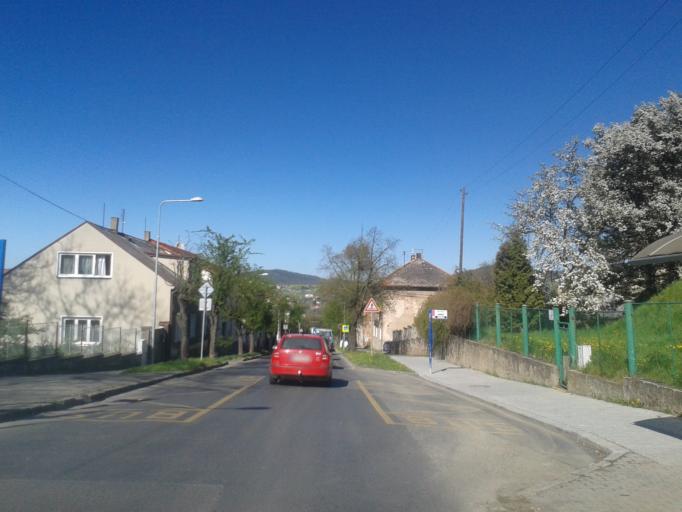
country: CZ
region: Central Bohemia
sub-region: Okres Beroun
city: Beroun
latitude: 49.9534
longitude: 14.0713
